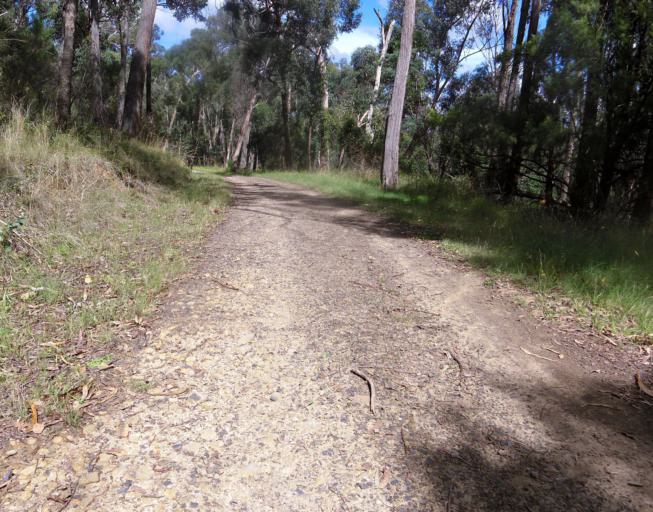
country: AU
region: Victoria
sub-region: Yarra Ranges
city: Montrose
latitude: -37.8288
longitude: 145.3425
